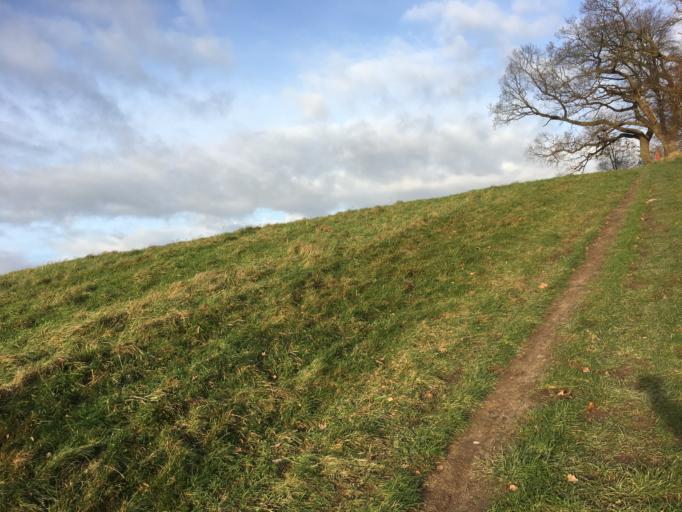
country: DK
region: Capital Region
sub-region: Fureso Kommune
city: Farum
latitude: 55.7925
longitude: 12.3417
